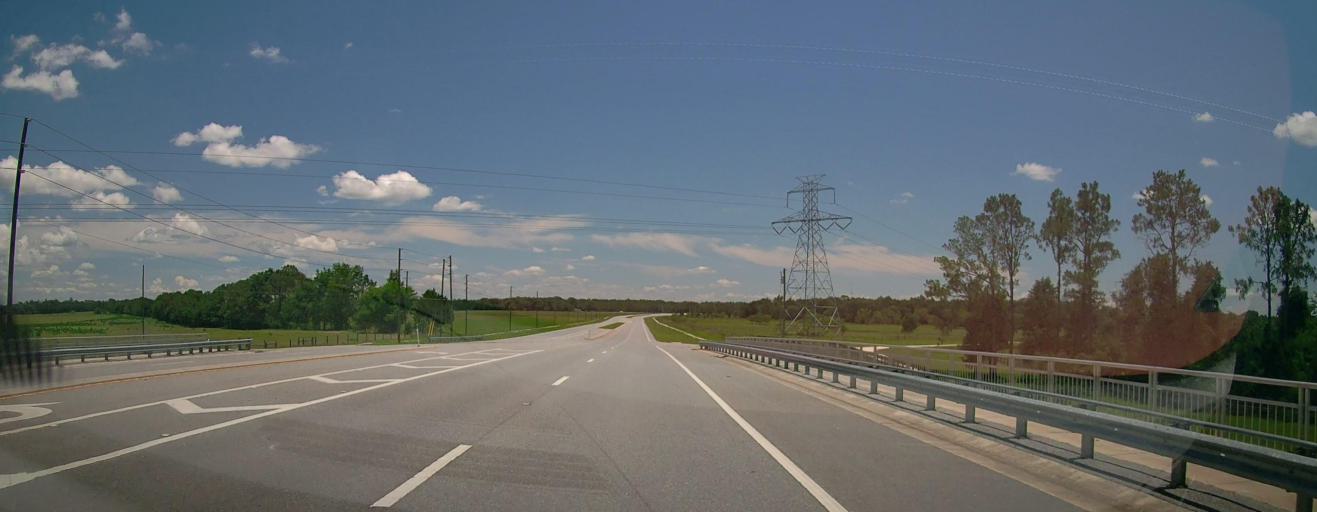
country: US
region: Florida
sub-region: Marion County
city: Silver Springs Shores
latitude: 29.0704
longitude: -82.0254
